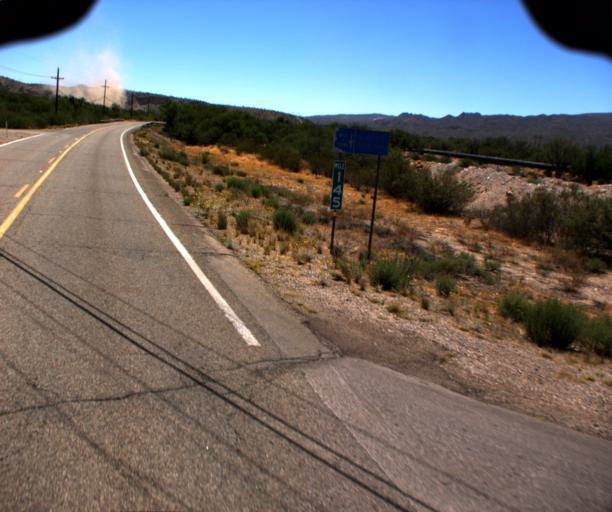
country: US
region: Arizona
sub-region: Pinal County
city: Kearny
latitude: 33.0500
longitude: -110.8917
